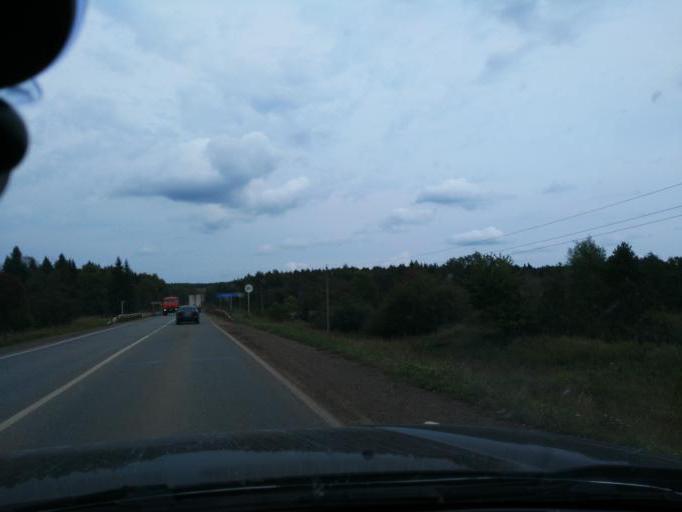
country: RU
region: Perm
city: Kuyeda
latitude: 56.4554
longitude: 55.6193
